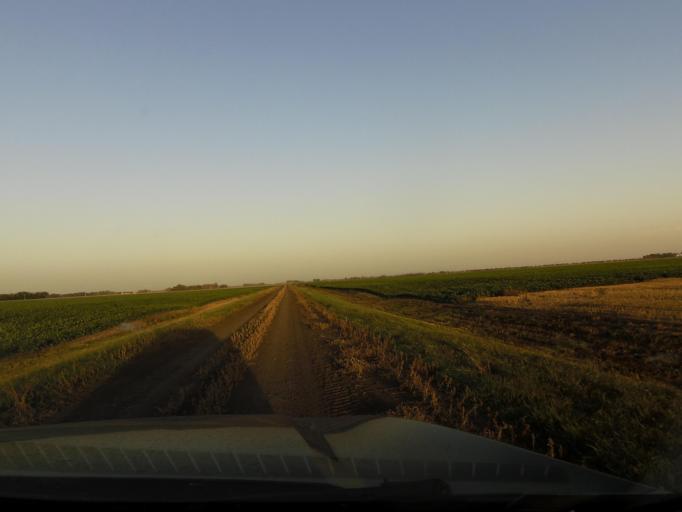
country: US
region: North Dakota
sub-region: Walsh County
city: Grafton
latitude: 48.3833
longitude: -97.2452
